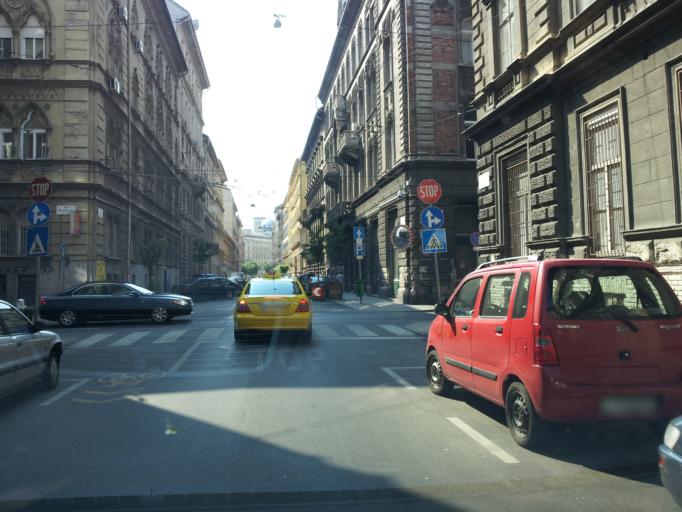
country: HU
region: Budapest
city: Budapest VII. keruelet
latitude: 47.5001
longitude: 19.0674
